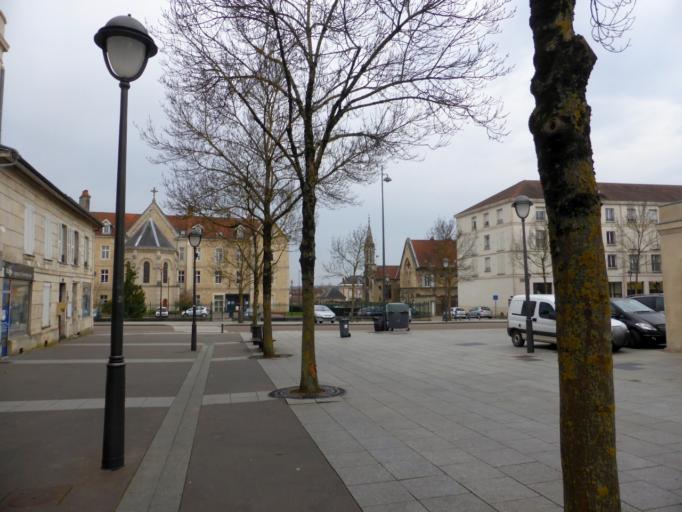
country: FR
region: Champagne-Ardenne
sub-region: Departement de la Haute-Marne
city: Saint-Dizier
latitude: 48.6369
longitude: 4.9476
